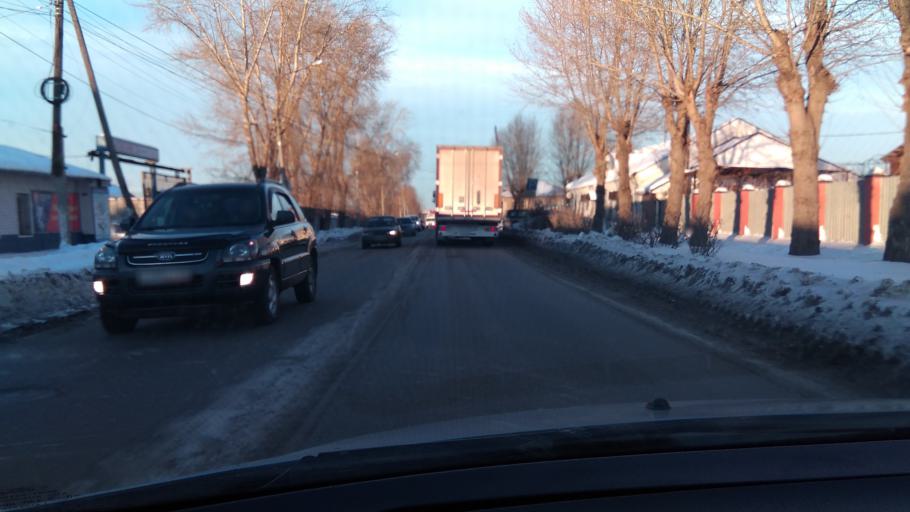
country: RU
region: Sverdlovsk
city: Sovkhoznyy
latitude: 56.7630
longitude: 60.6277
